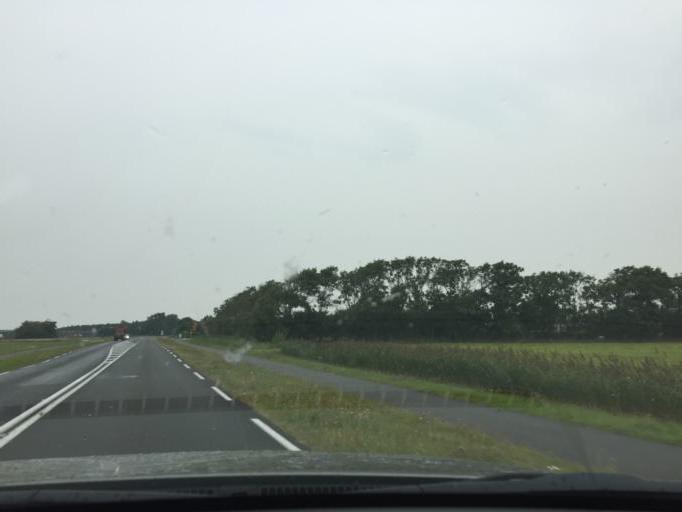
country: NL
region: North Holland
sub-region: Gemeente Texel
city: Den Burg
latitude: 53.0672
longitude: 4.7747
